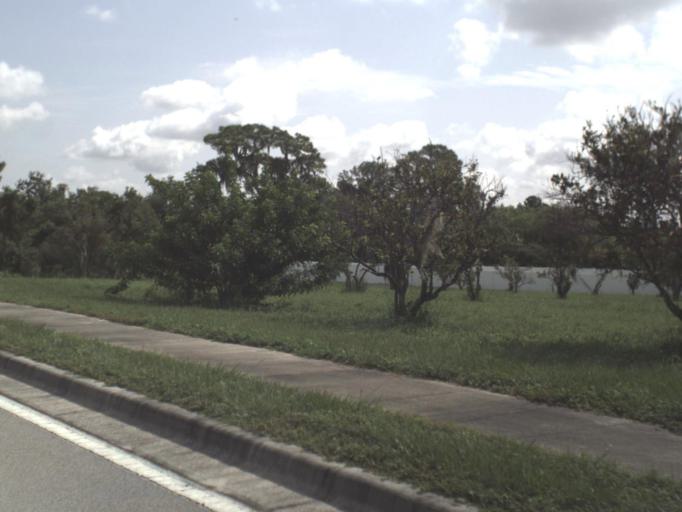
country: US
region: Florida
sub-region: Polk County
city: Jan-Phyl Village
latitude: 28.0024
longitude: -81.7543
